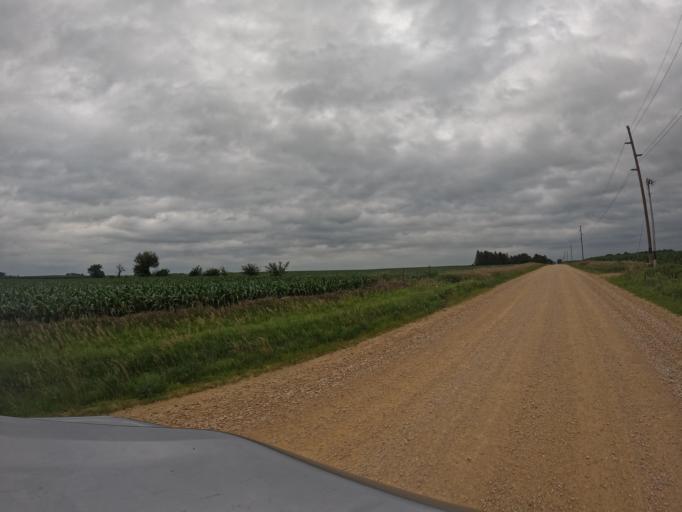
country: US
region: Iowa
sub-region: Clinton County
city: De Witt
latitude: 41.7863
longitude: -90.4621
